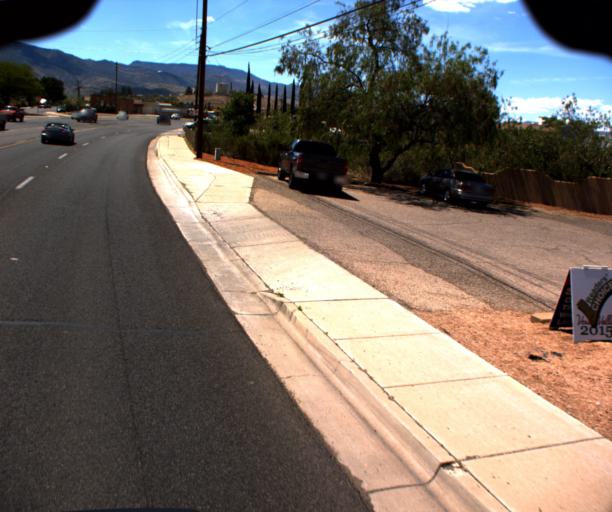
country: US
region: Arizona
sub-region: Yavapai County
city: Cottonwood
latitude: 34.7287
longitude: -112.0193
